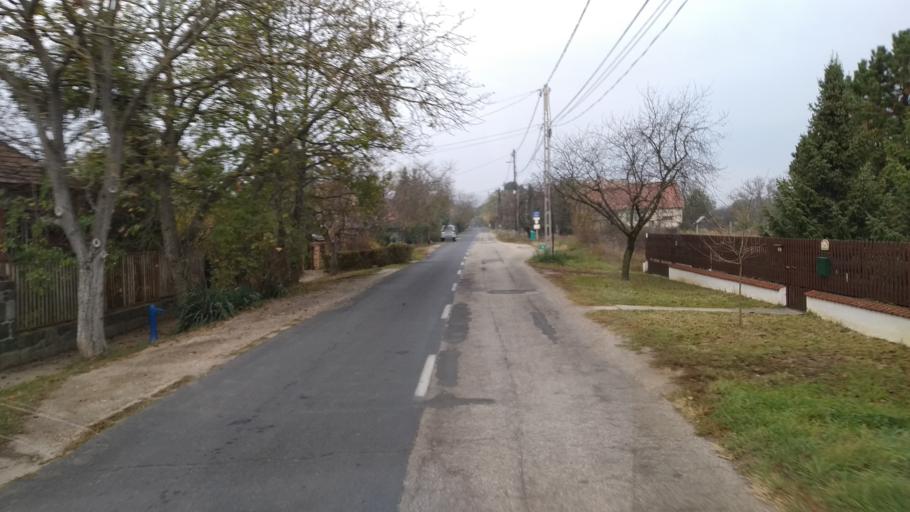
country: HU
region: Pest
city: Veroce
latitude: 47.8053
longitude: 19.0191
